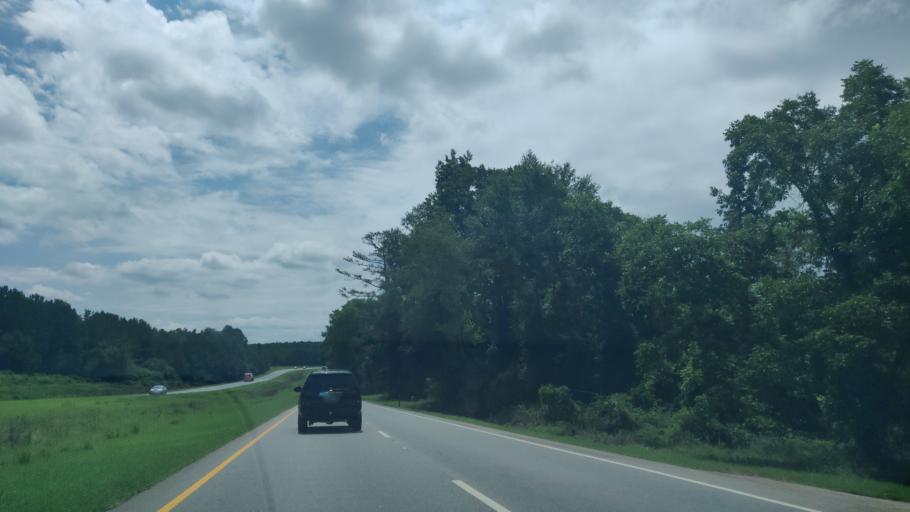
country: US
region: Georgia
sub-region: Terrell County
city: Dawson
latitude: 31.8709
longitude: -84.4914
